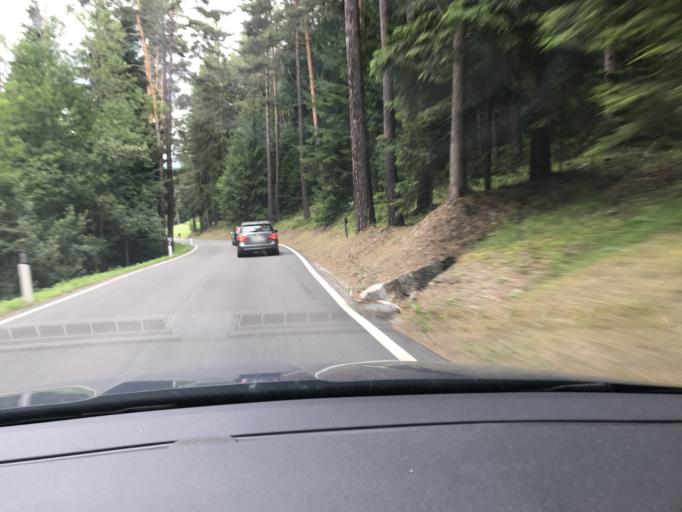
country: IT
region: Trentino-Alto Adige
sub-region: Bolzano
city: Bressanone
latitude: 46.6887
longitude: 11.6791
